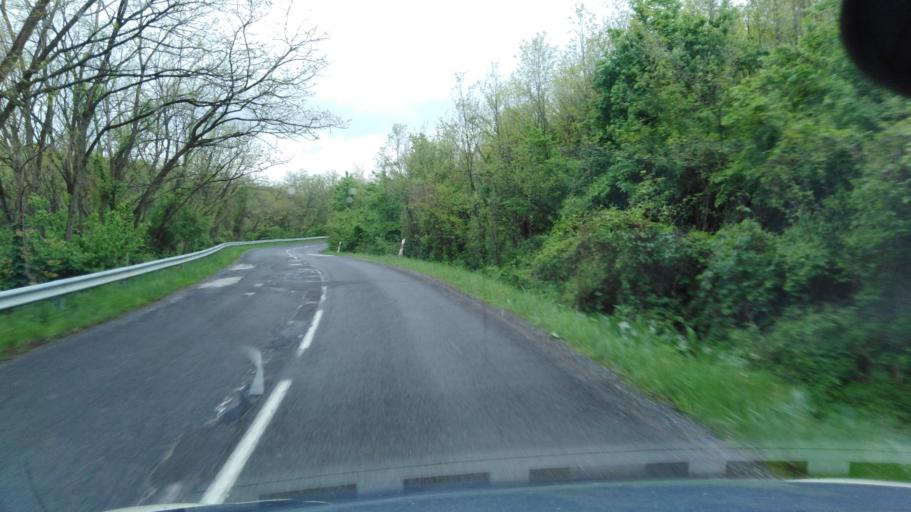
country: HU
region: Nograd
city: Rimoc
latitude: 48.0224
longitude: 19.5908
